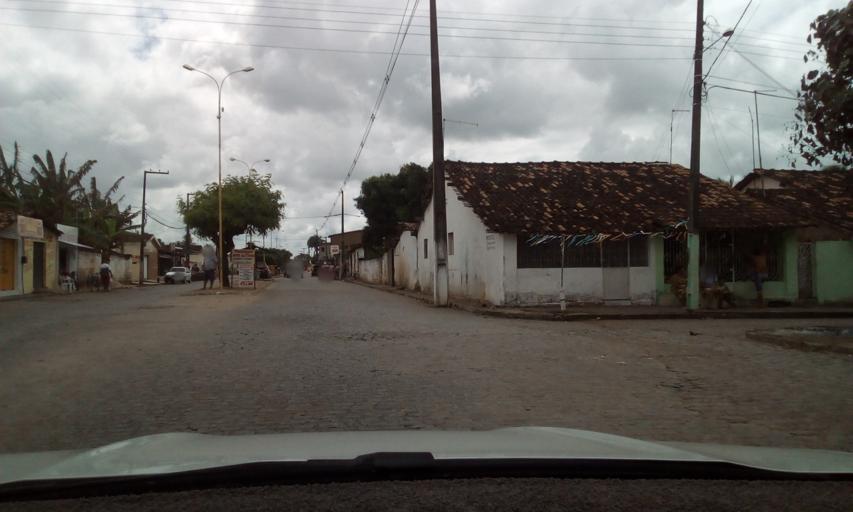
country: BR
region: Paraiba
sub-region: Rio Tinto
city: Rio Tinto
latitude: -6.7915
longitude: -35.0679
